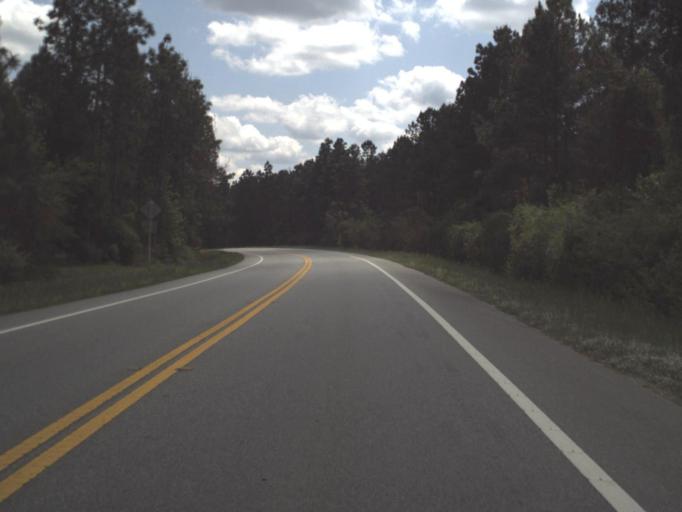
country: US
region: Florida
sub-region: Escambia County
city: Molino
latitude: 30.8232
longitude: -87.4356
